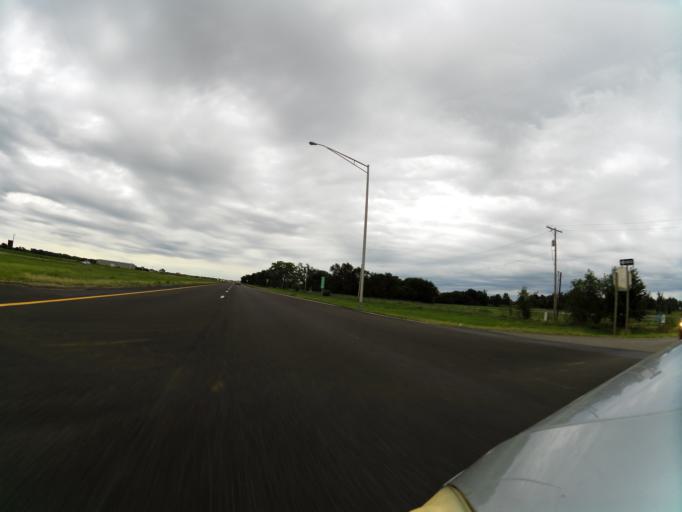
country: US
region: Kansas
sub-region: Reno County
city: Haven
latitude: 37.8763
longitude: -97.6656
